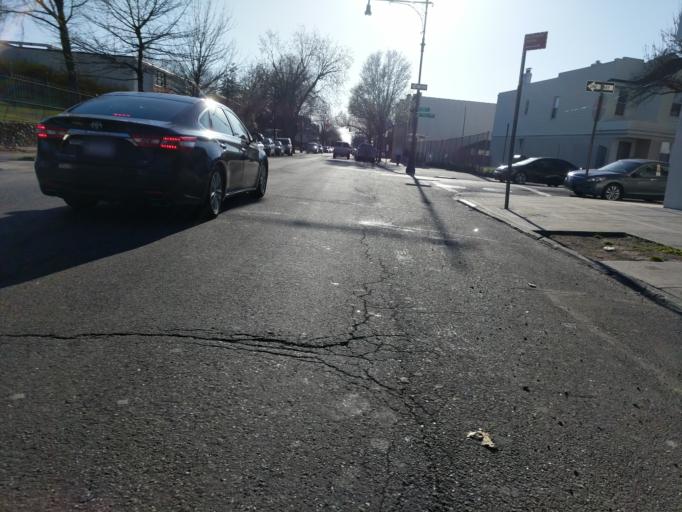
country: US
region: New York
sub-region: Kings County
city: East New York
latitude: 40.7025
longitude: -73.8742
